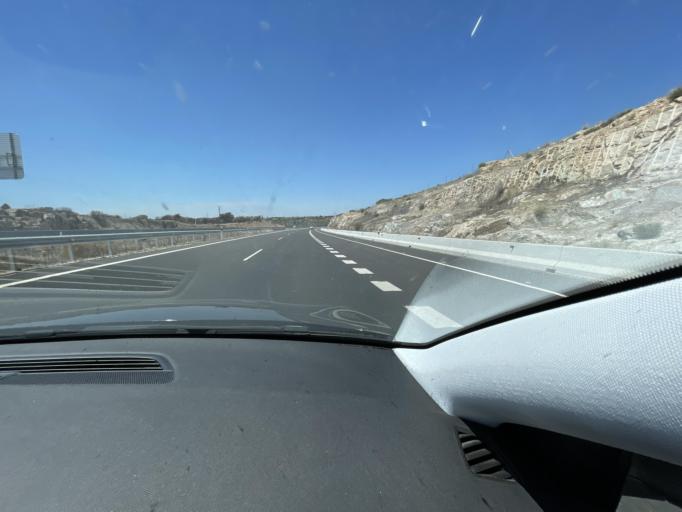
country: ES
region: Castille and Leon
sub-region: Provincia de Salamanca
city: Fuentes de Onoro
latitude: 40.5946
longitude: -6.8029
